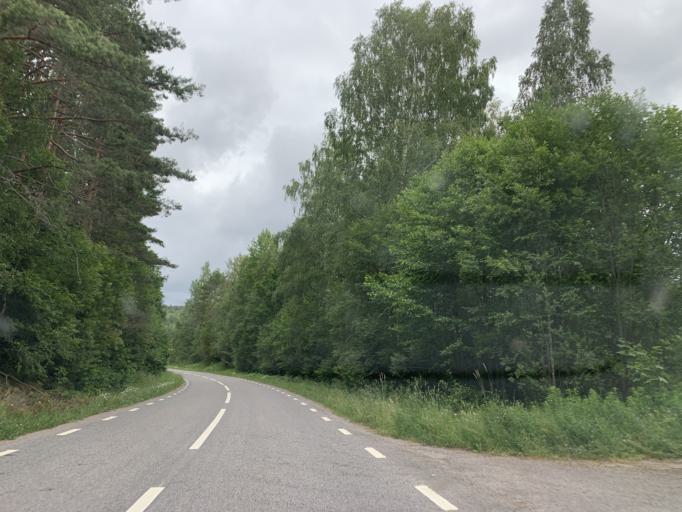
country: SE
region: Kalmar
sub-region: Vasterviks Kommun
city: Overum
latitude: 58.0115
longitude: 16.1729
